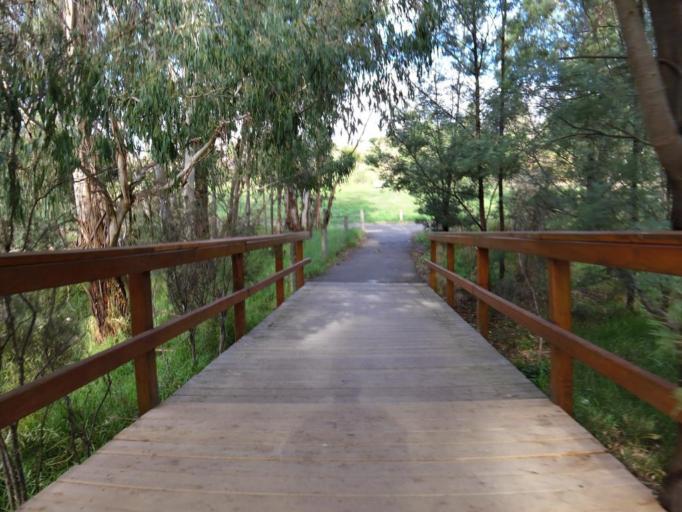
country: AU
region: Victoria
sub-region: Manningham
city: Doncaster
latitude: -37.7744
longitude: 145.1349
